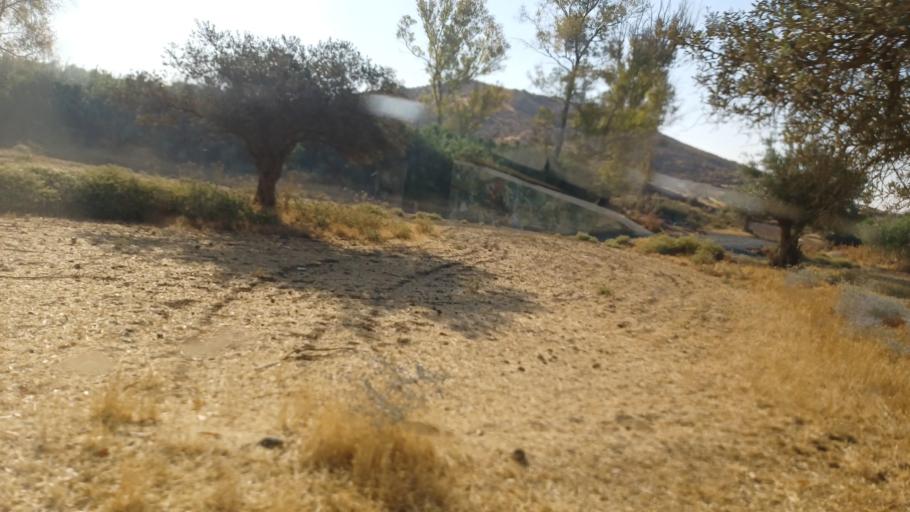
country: CY
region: Lefkosia
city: Lympia
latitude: 34.9872
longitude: 33.4373
